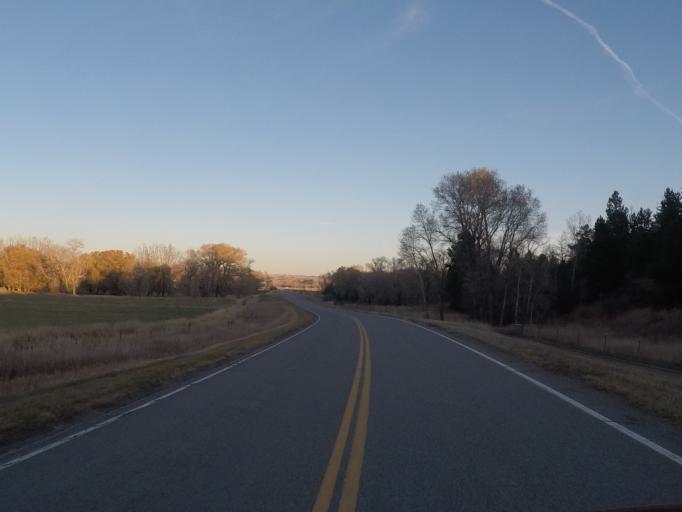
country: US
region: Montana
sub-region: Sweet Grass County
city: Big Timber
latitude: 45.7847
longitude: -109.8431
